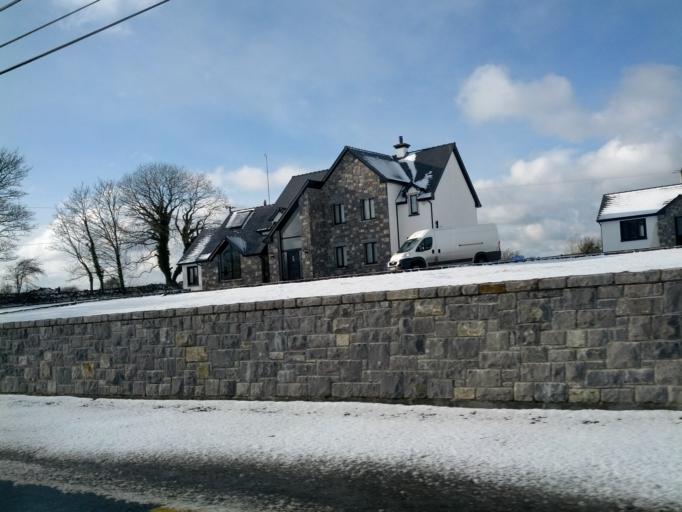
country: IE
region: Connaught
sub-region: County Galway
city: Athenry
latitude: 53.2190
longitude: -8.7485
